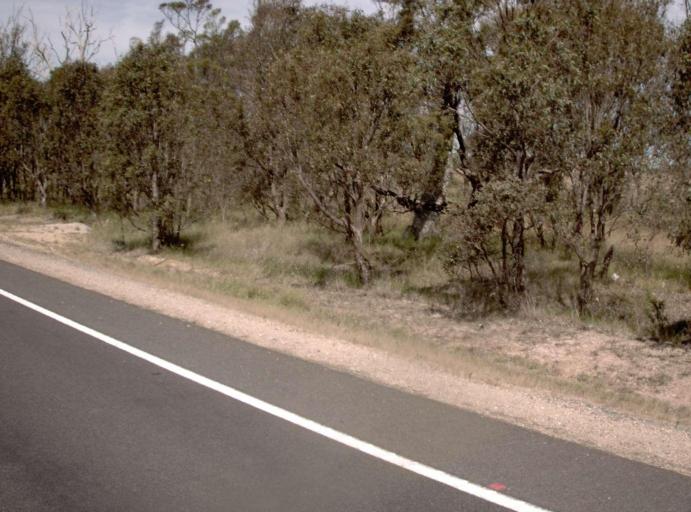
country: AU
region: Victoria
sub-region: East Gippsland
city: Bairnsdale
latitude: -37.8946
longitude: 147.3737
